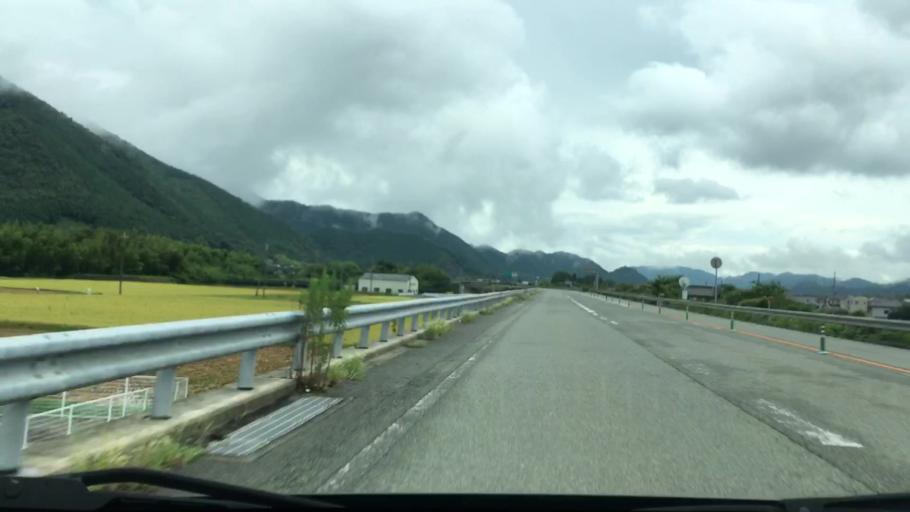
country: JP
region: Hyogo
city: Yamazakicho-nakabirose
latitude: 35.0534
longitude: 134.7638
